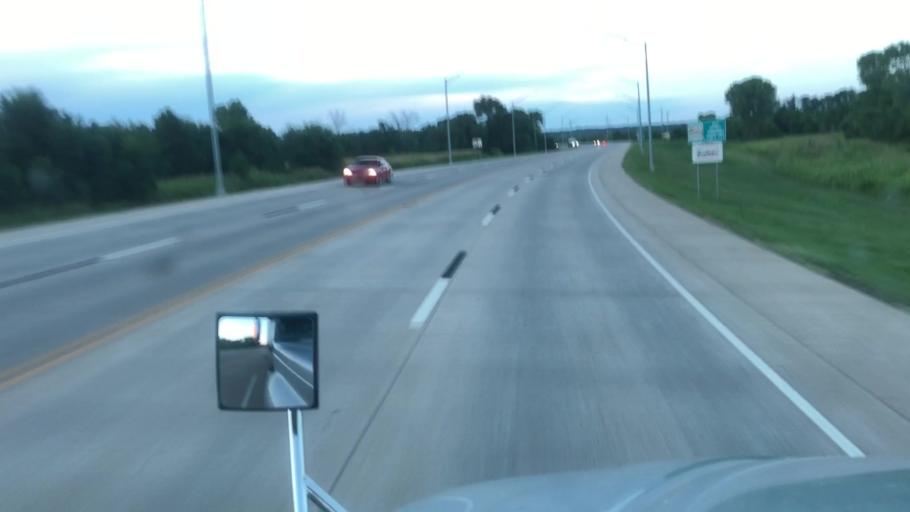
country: US
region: Oklahoma
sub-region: Kay County
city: Ponca City
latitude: 36.6855
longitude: -97.0695
